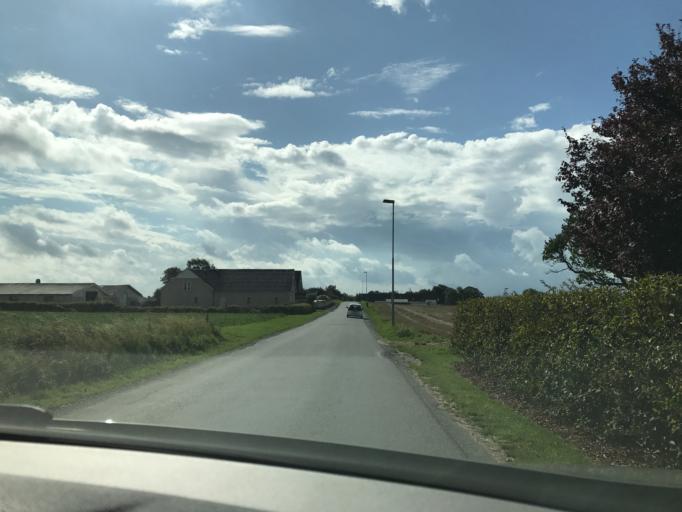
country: DK
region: South Denmark
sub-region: Middelfart Kommune
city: Norre Aby
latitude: 55.4394
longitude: 9.8269
